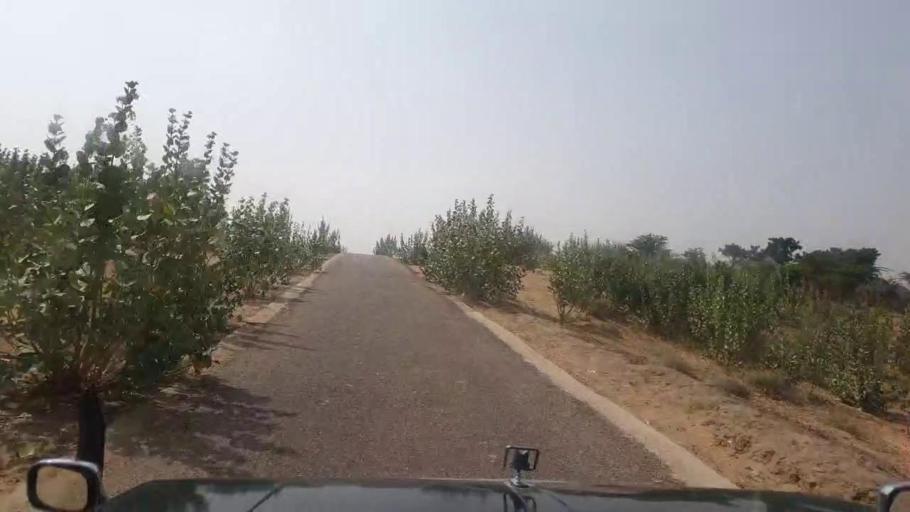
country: PK
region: Sindh
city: Islamkot
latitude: 25.0831
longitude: 70.1549
